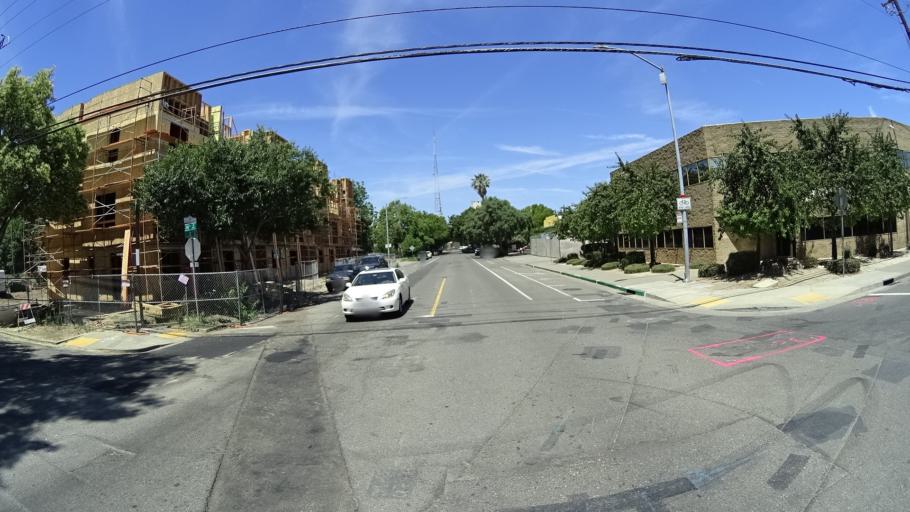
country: US
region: California
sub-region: Sacramento County
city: Sacramento
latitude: 38.5864
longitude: -121.4845
